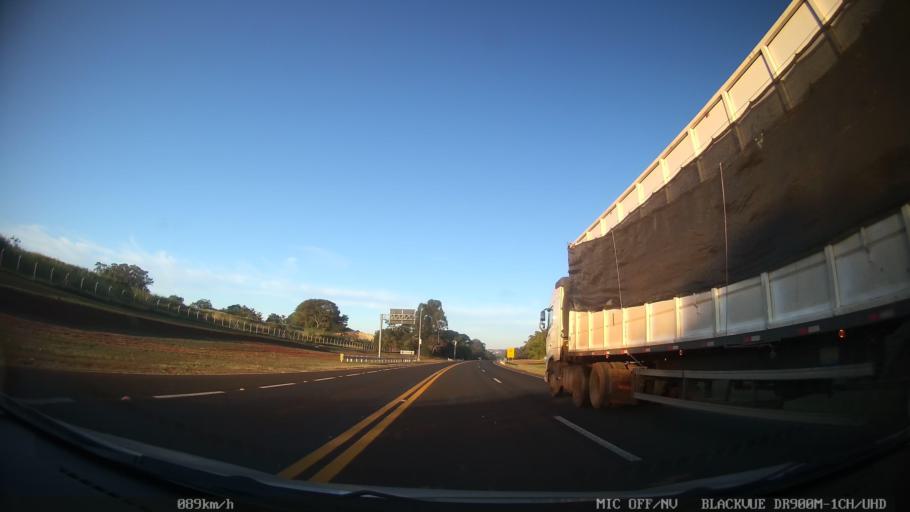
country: BR
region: Sao Paulo
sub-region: Araraquara
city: Araraquara
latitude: -21.8168
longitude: -48.2035
